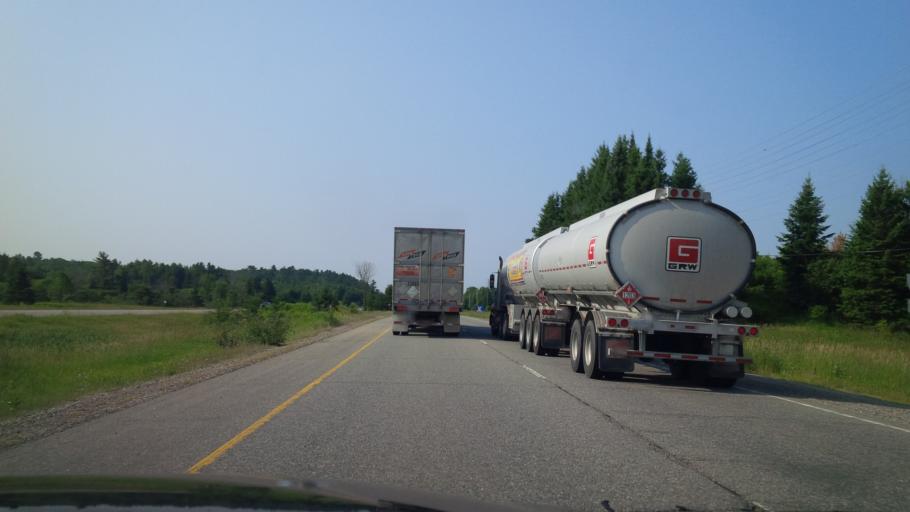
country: CA
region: Ontario
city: Huntsville
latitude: 45.2551
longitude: -79.2968
